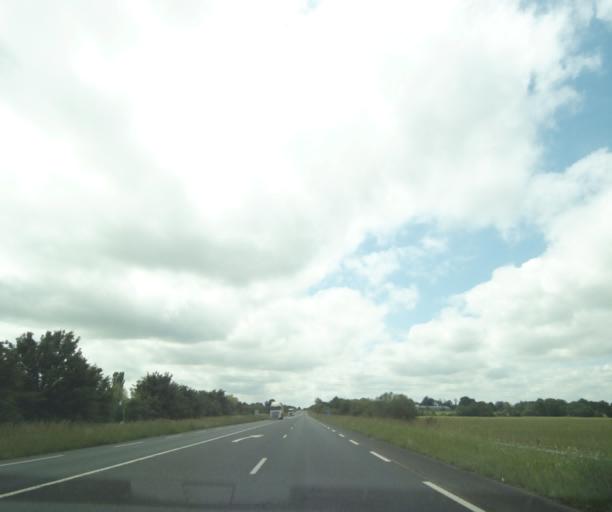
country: FR
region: Poitou-Charentes
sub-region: Departement des Deux-Sevres
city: Airvault
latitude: 46.7883
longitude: -0.2153
